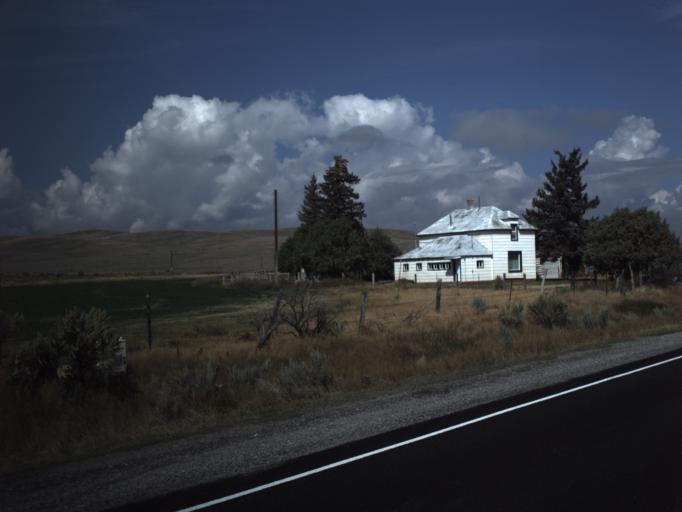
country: US
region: Utah
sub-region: Rich County
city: Randolph
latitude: 41.5988
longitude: -111.1748
